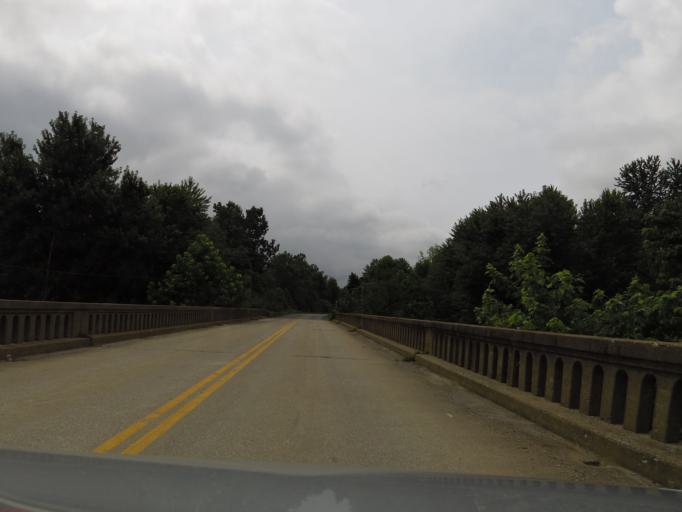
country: US
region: Kentucky
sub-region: Hopkins County
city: Madisonville
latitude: 37.3173
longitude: -87.3692
